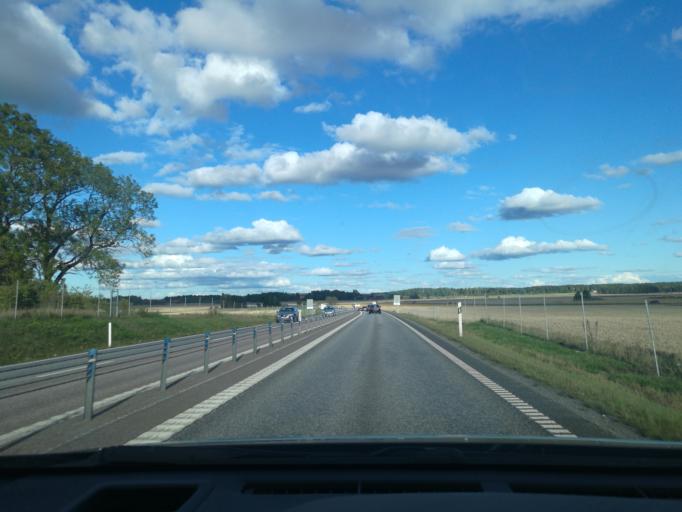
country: SE
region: Vaestmanland
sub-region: Kopings Kommun
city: Koping
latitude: 59.5532
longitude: 16.0387
